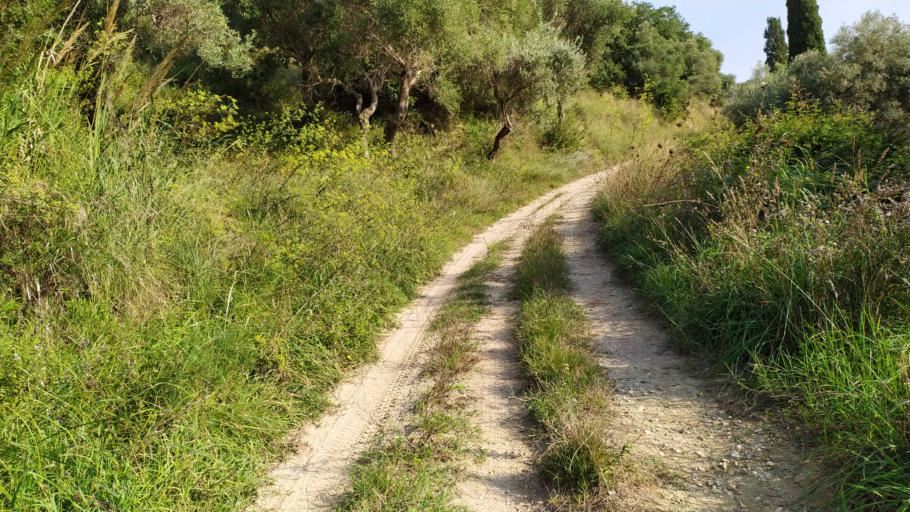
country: IT
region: Sicily
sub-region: Messina
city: Condro
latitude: 38.1611
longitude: 15.3343
